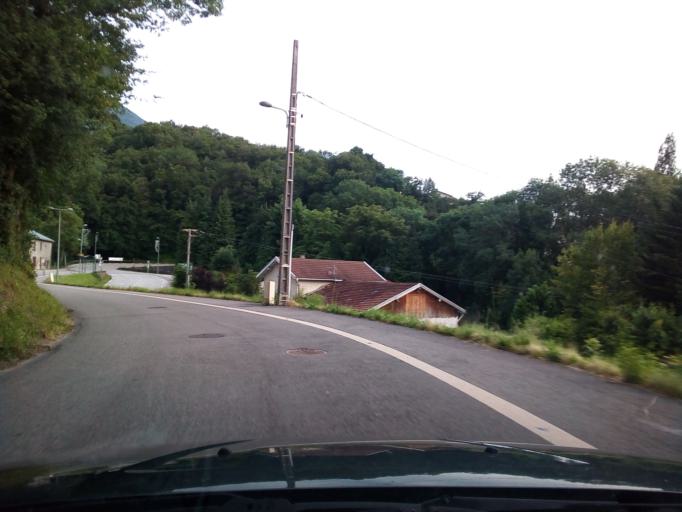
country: FR
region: Rhone-Alpes
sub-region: Departement de l'Isere
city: Saint-Georges-de-Commiers
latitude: 45.0395
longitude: 5.7055
